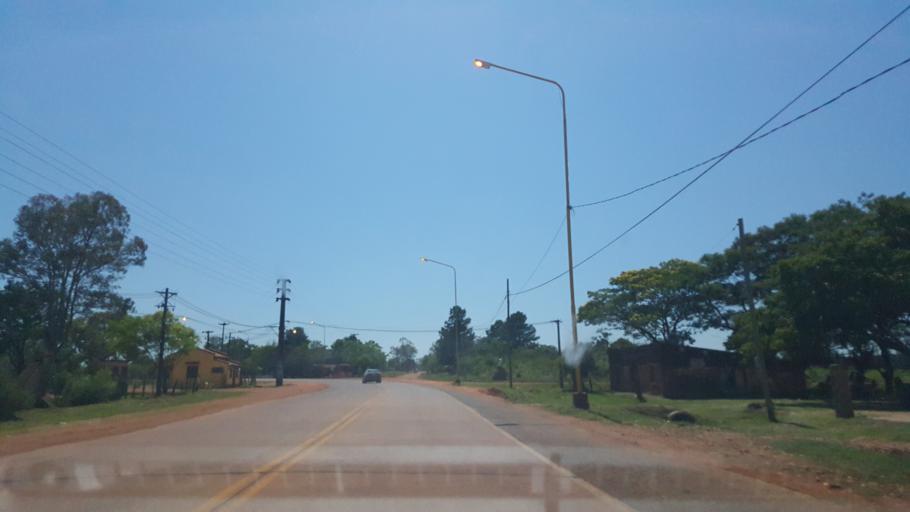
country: AR
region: Corrientes
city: Santo Tome
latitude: -28.5510
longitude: -56.0677
